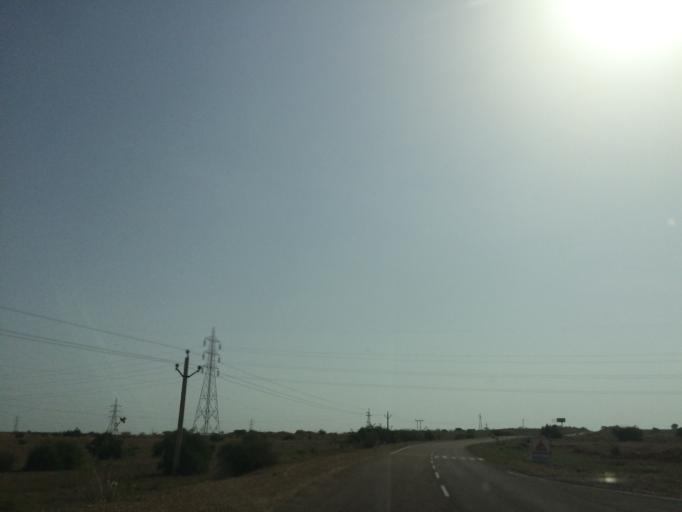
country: IN
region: Rajasthan
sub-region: Jaisalmer
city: Jaisalmer
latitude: 26.9195
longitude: 70.8078
